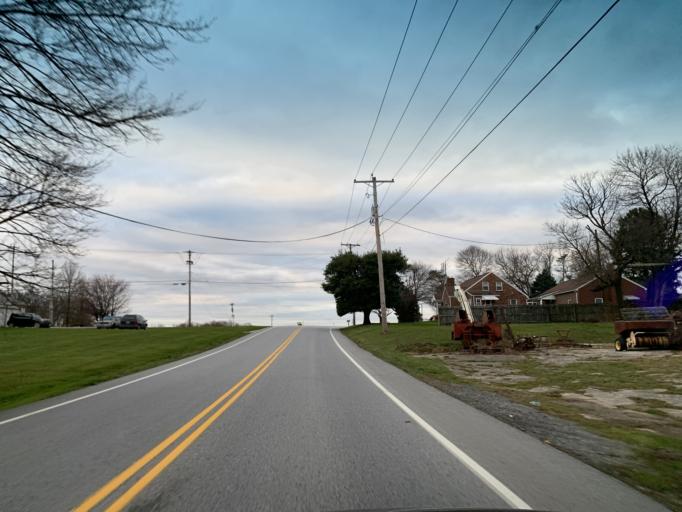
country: US
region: Pennsylvania
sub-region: York County
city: Shrewsbury
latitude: 39.7821
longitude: -76.6327
